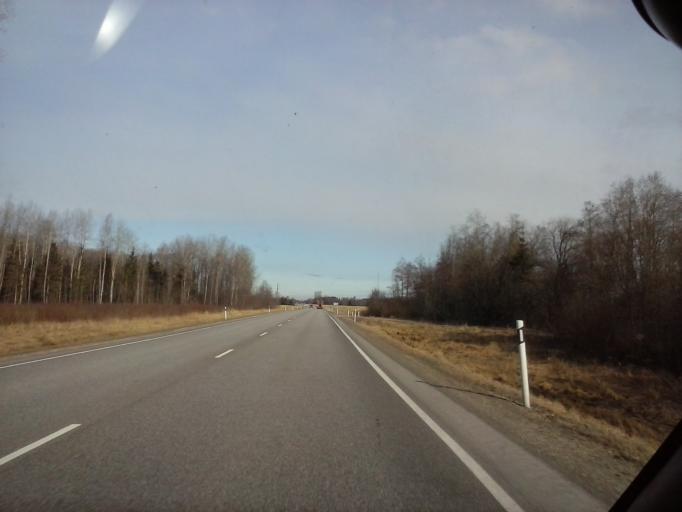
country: EE
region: Jaervamaa
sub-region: Paide linn
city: Paide
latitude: 58.8177
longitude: 25.7556
